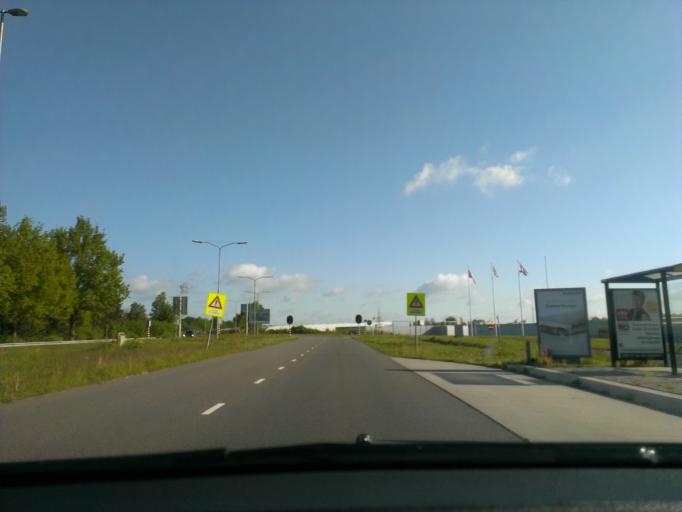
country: NL
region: Drenthe
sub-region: Gemeente Emmen
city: Emmen
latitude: 52.7619
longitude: 6.8983
